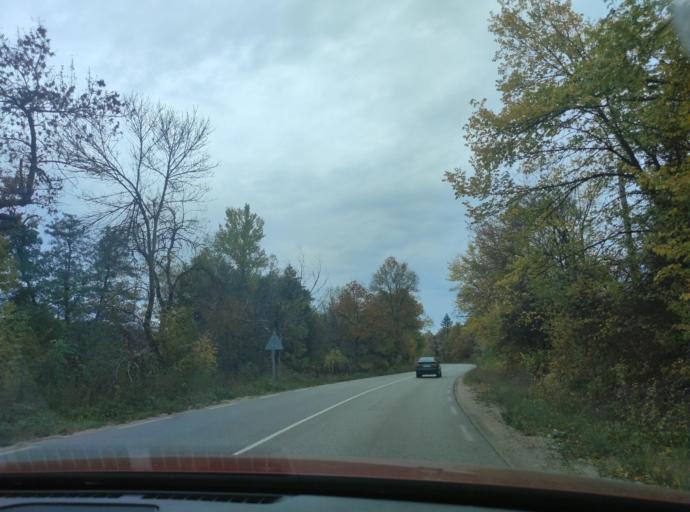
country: BG
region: Montana
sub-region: Obshtina Berkovitsa
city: Berkovitsa
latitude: 43.2665
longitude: 23.1755
